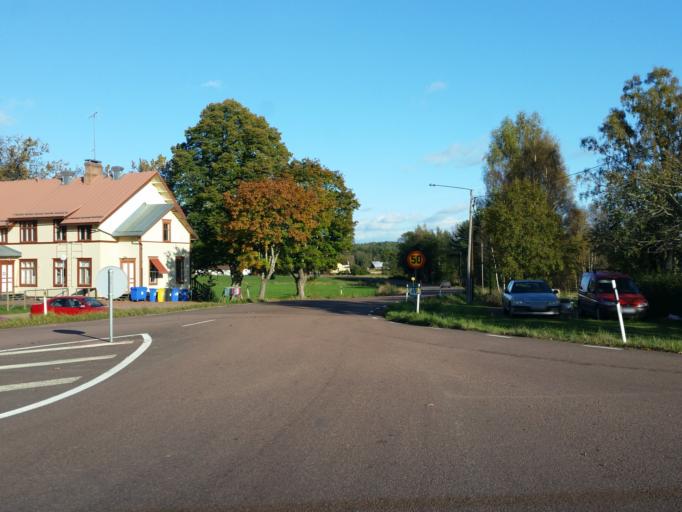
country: AX
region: Mariehamns stad
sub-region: Mariehamn
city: Mariehamn
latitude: 60.1314
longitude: 19.8437
